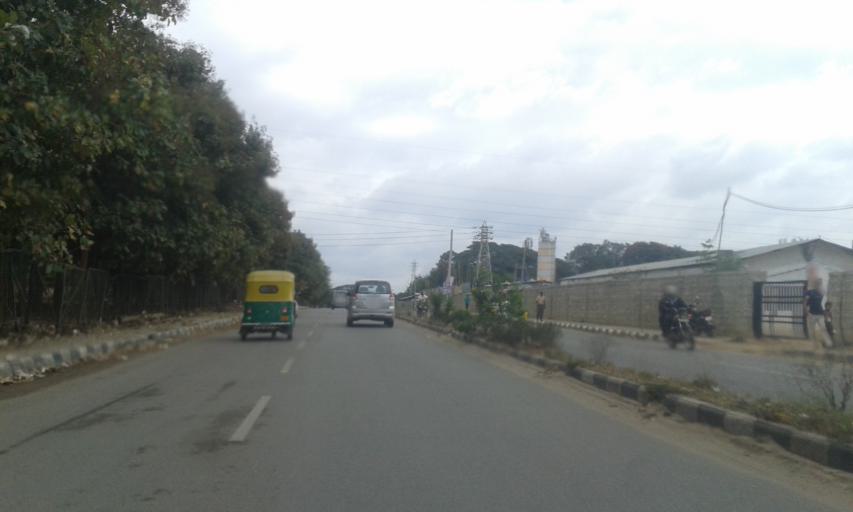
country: IN
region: Karnataka
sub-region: Bangalore Urban
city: Bangalore
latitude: 12.9686
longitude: 77.6604
